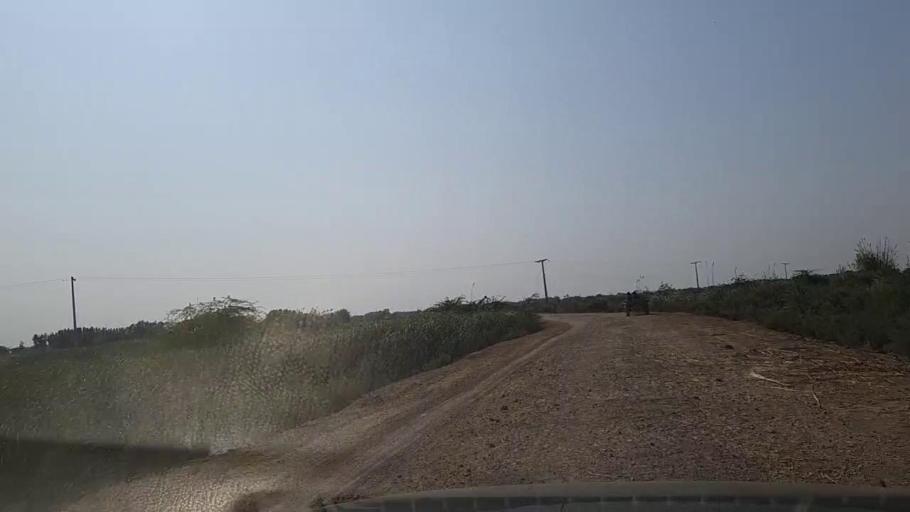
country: PK
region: Sindh
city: Mirpur Sakro
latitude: 24.3678
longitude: 67.6466
